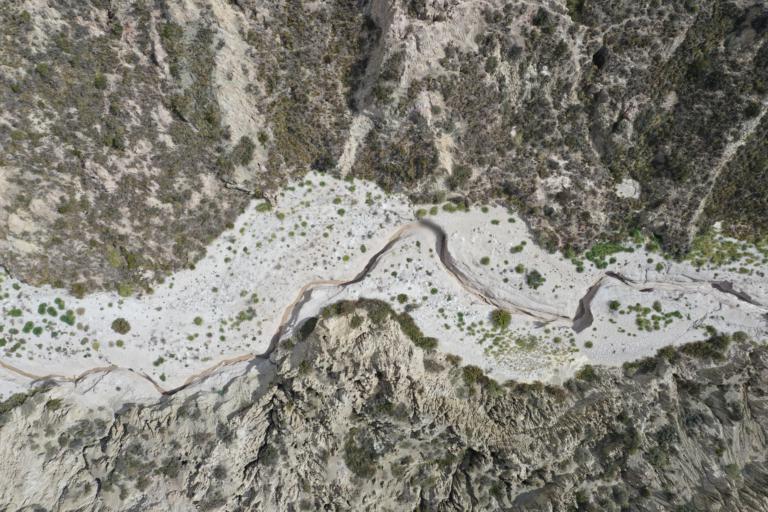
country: BO
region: La Paz
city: La Paz
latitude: -16.5639
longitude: -68.1226
